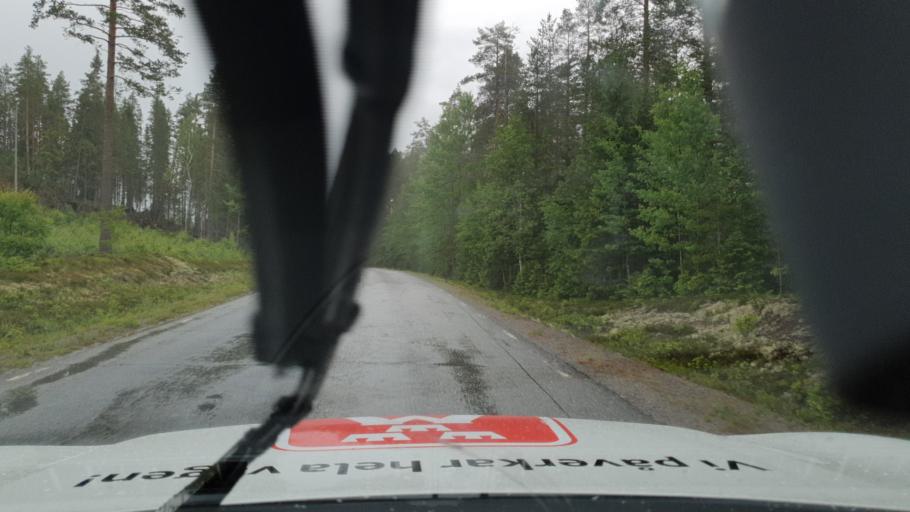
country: SE
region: Vaesterbotten
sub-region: Nordmalings Kommun
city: Nordmaling
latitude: 63.8070
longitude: 19.5031
